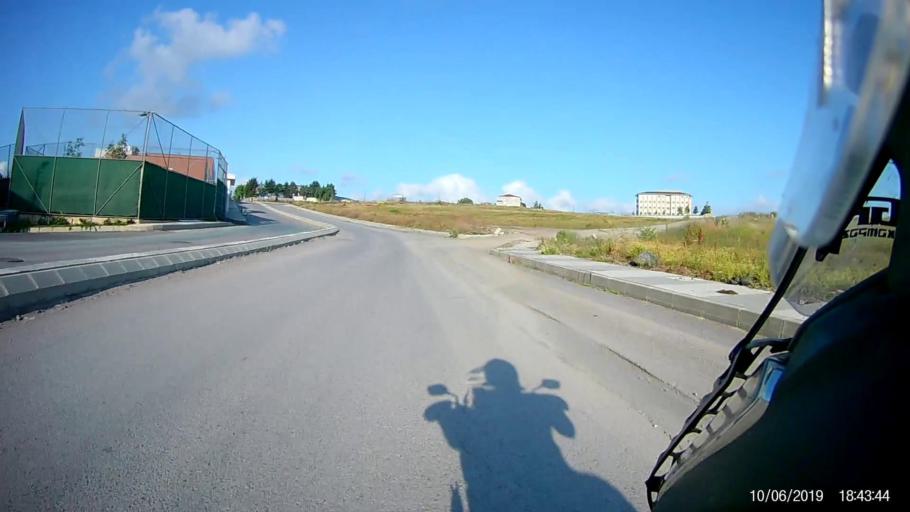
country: TR
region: Istanbul
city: Sancaktepe
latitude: 41.0373
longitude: 29.2659
